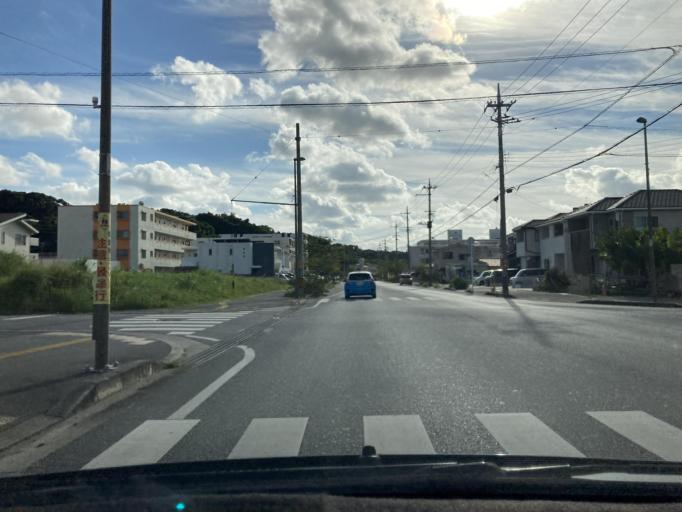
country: JP
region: Okinawa
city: Itoman
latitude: 26.1222
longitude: 127.6735
